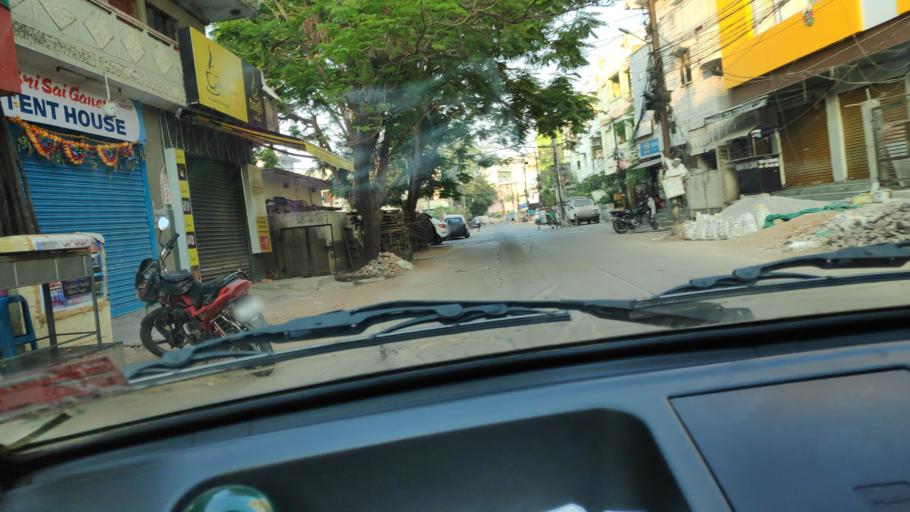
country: IN
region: Telangana
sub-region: Rangareddi
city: Gaddi Annaram
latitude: 17.3624
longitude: 78.5252
